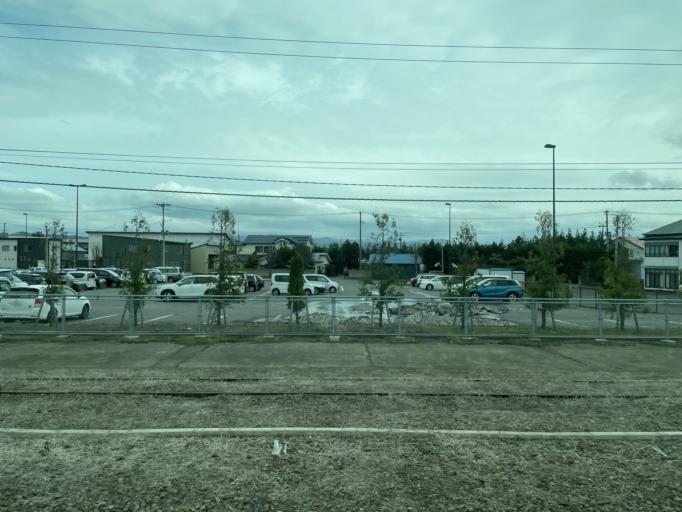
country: JP
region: Aomori
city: Namioka
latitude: 40.7095
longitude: 140.5801
